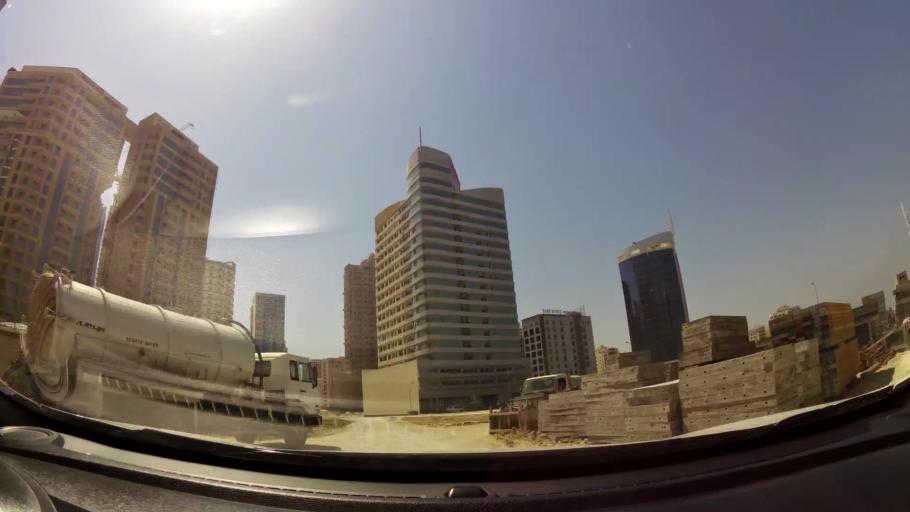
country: BH
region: Manama
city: Manama
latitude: 26.2219
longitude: 50.6059
